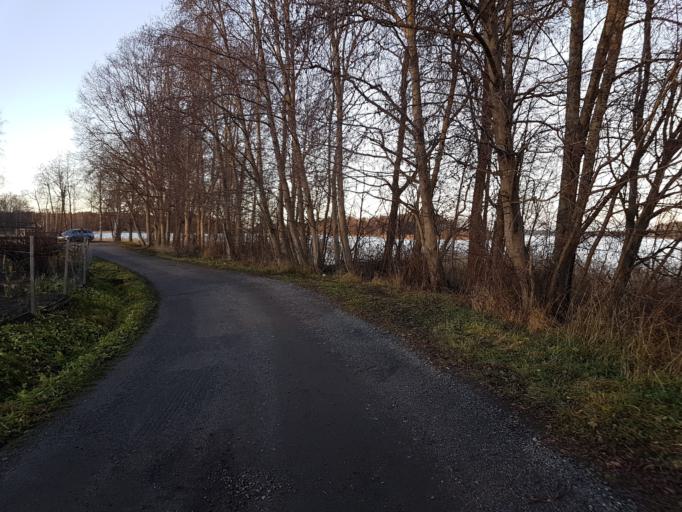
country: FI
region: Northern Savo
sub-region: Kuopio
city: Kuopio
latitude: 62.9297
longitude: 27.6254
